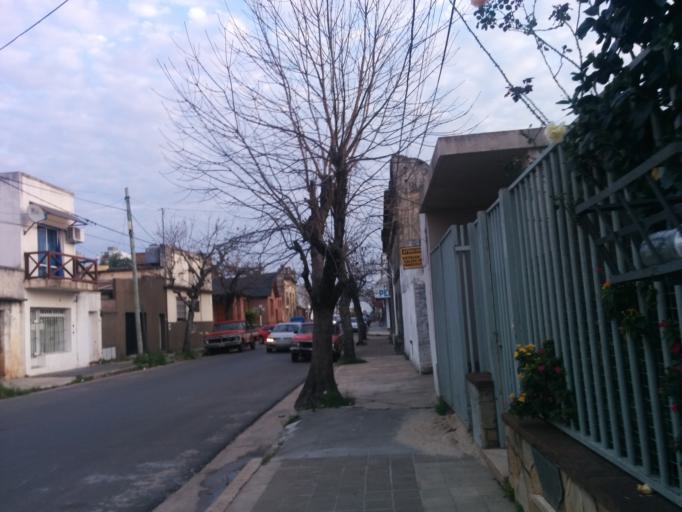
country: AR
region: Entre Rios
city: Concordia
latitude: -31.3895
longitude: -58.0204
